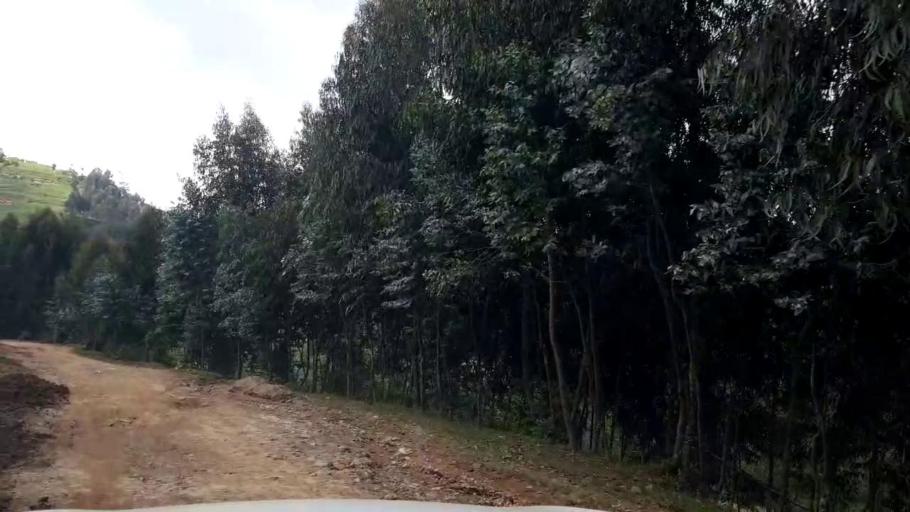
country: RW
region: Western Province
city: Kibuye
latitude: -1.8916
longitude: 29.4661
